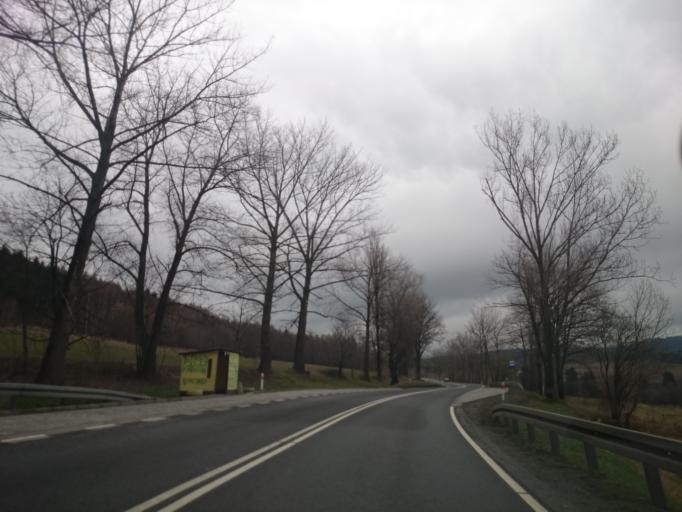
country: PL
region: Lower Silesian Voivodeship
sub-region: Powiat zabkowicki
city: Bardo
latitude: 50.4321
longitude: 16.7530
